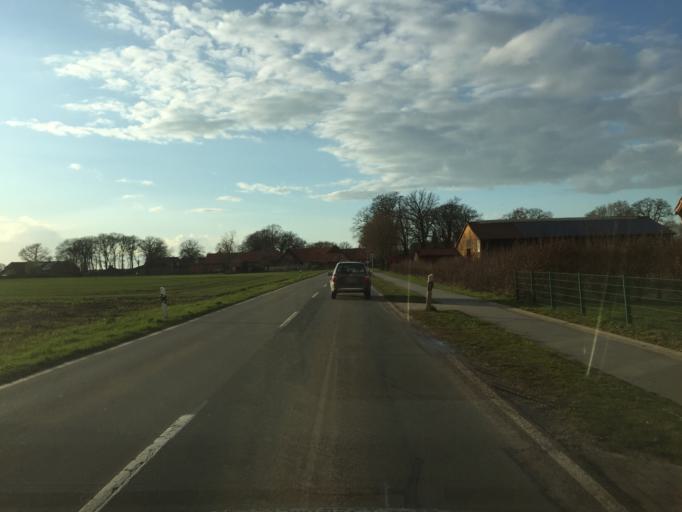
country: DE
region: Lower Saxony
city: Steyerberg
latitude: 52.5676
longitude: 8.9995
